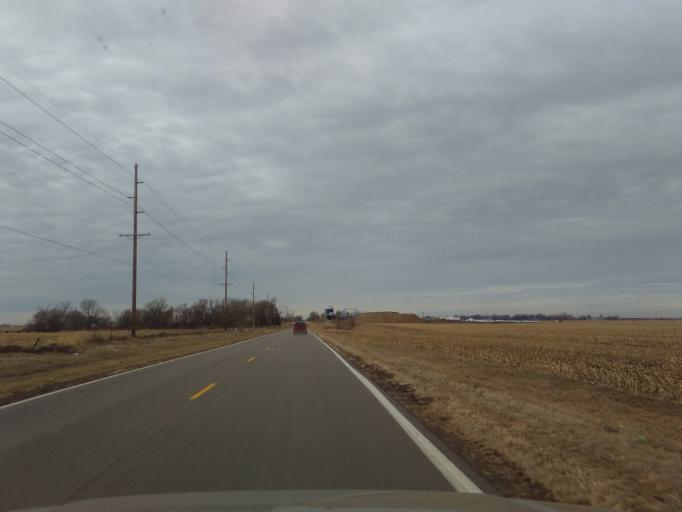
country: US
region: Nebraska
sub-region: Hall County
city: Grand Island
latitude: 40.7710
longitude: -98.3469
